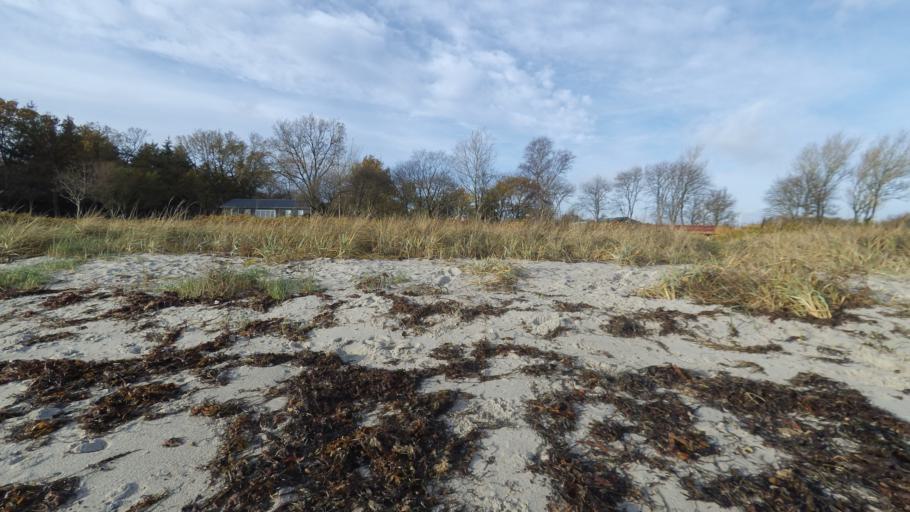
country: DK
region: Central Jutland
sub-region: Odder Kommune
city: Odder
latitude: 55.9246
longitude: 10.2571
